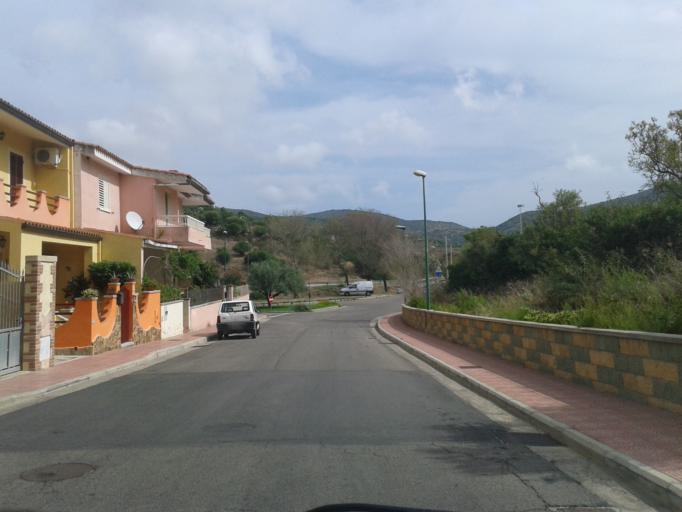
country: IT
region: Sardinia
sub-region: Provincia di Cagliari
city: Villasimius
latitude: 39.1447
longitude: 9.5242
